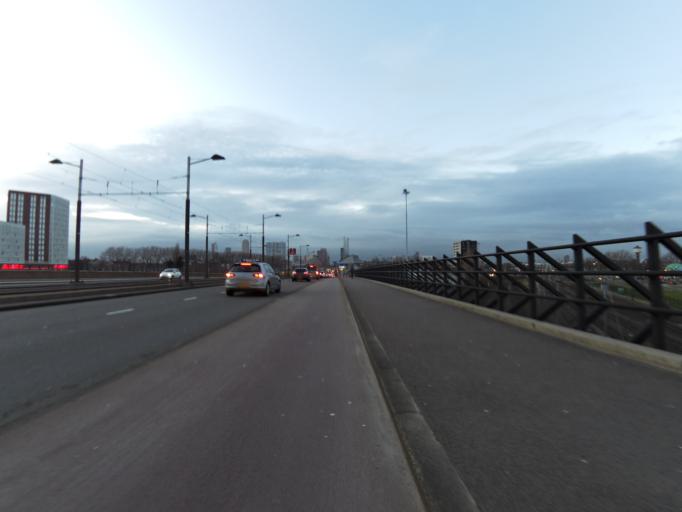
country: NL
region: South Holland
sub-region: Gemeente Rotterdam
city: Rotterdam
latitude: 51.8994
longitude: 4.5143
